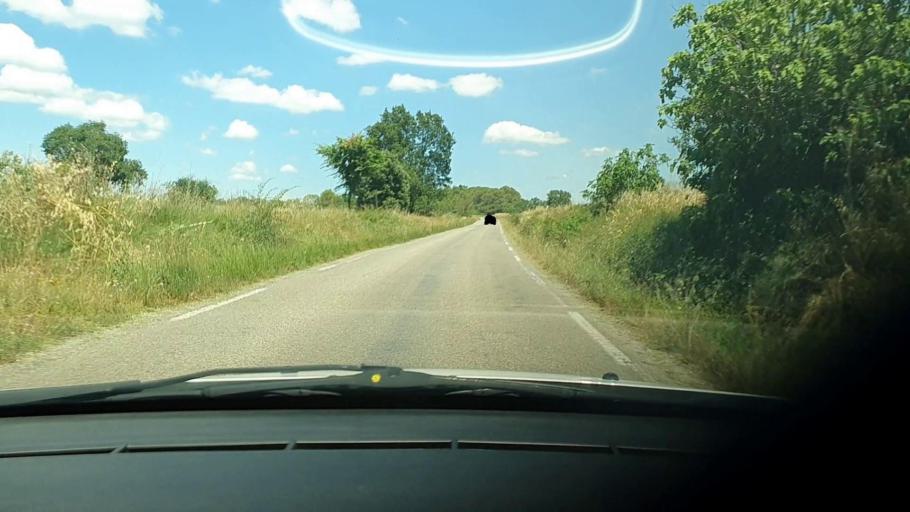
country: FR
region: Languedoc-Roussillon
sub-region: Departement du Gard
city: Blauzac
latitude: 43.9709
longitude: 4.3677
